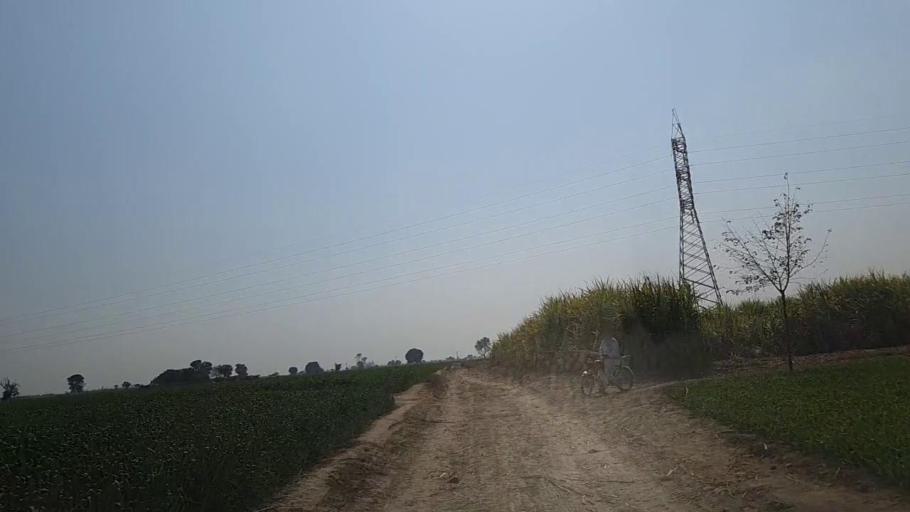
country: PK
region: Sindh
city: Moro
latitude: 26.6914
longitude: 67.9275
